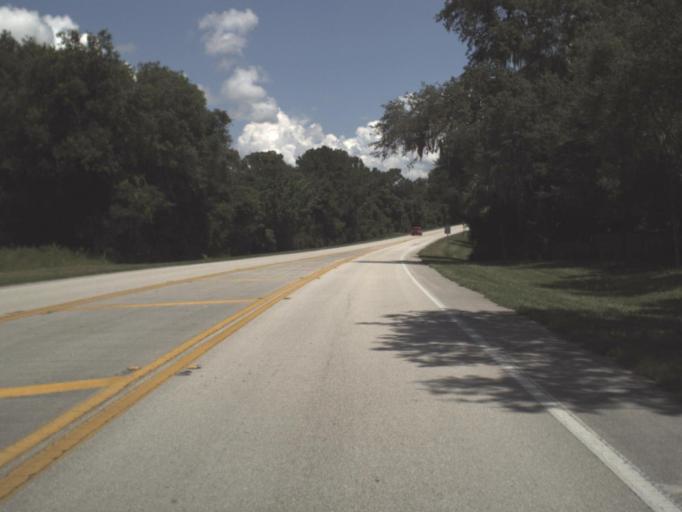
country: US
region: Florida
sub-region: Putnam County
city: Crescent City
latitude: 29.3661
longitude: -81.5086
